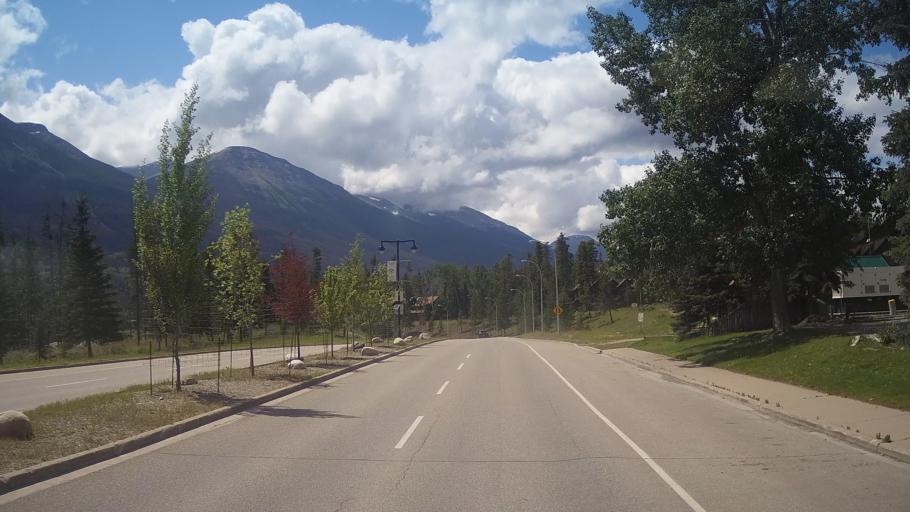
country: CA
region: Alberta
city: Jasper Park Lodge
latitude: 52.8705
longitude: -118.0919
